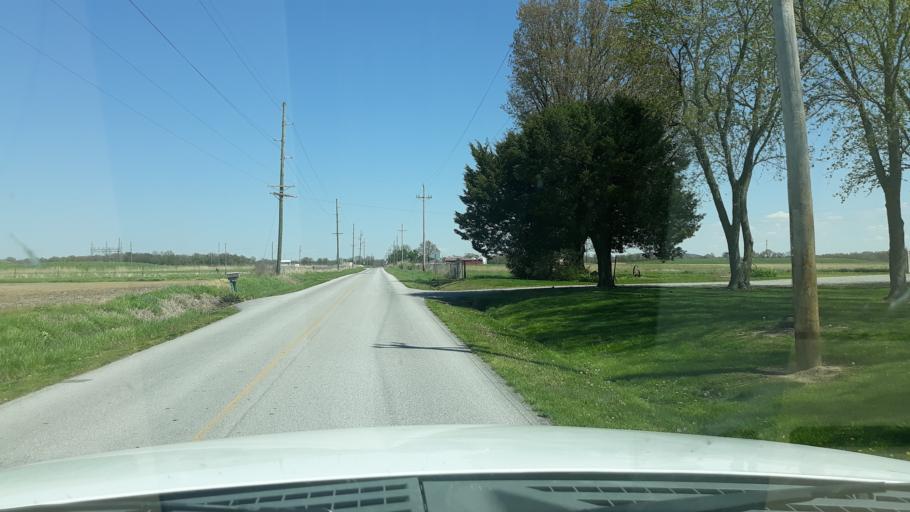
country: US
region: Illinois
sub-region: Saline County
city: Harrisburg
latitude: 37.8342
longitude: -88.6429
